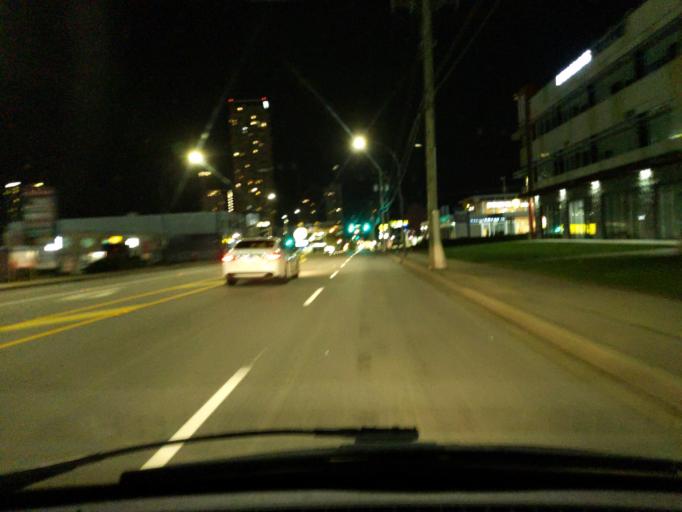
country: CA
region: British Columbia
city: New Westminster
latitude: 49.1916
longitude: -122.8401
